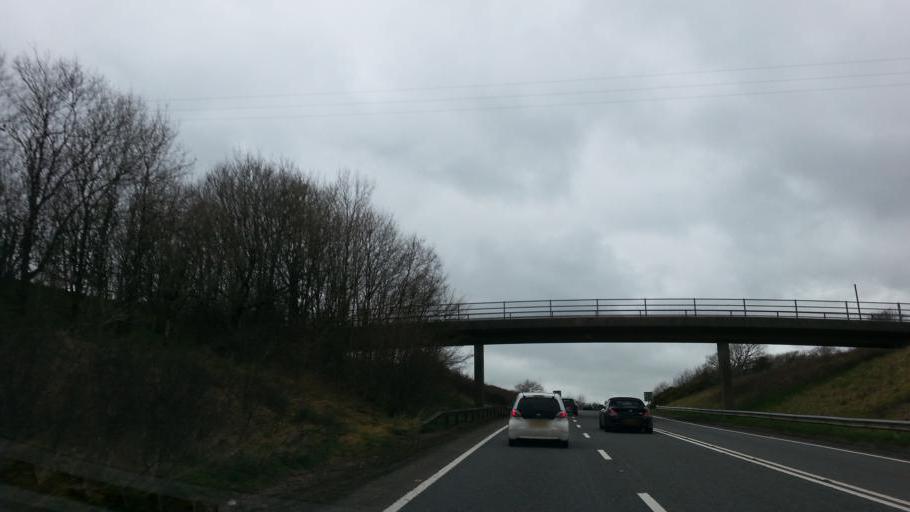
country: GB
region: England
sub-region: Devon
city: South Molton
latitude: 51.0031
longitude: -3.7457
